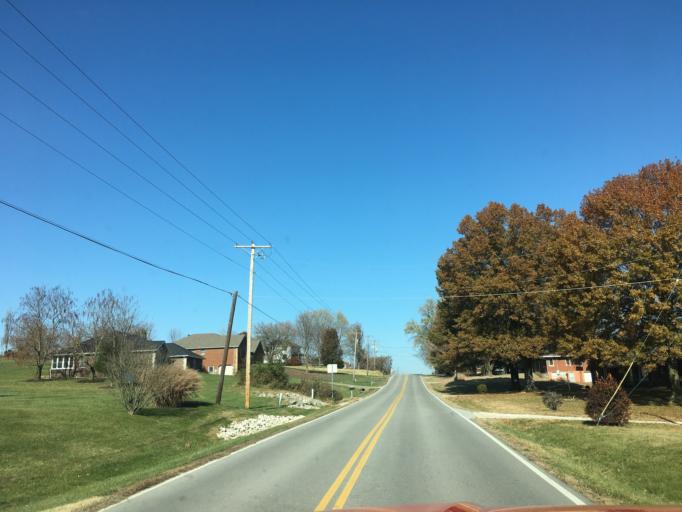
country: US
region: Missouri
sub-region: Cole County
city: Wardsville
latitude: 38.5084
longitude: -92.1756
